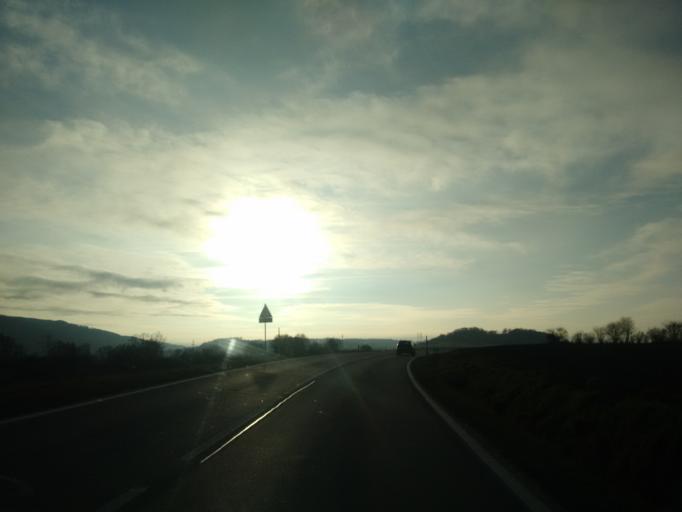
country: AT
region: Lower Austria
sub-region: Politischer Bezirk Melk
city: Leiben
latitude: 48.2144
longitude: 15.2840
